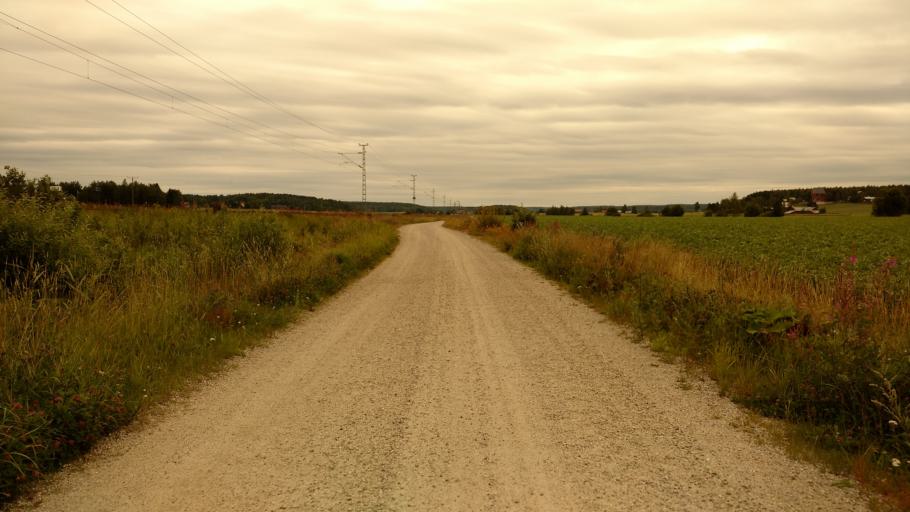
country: FI
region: Varsinais-Suomi
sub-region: Turku
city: Paimio
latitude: 60.4224
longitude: 22.8190
